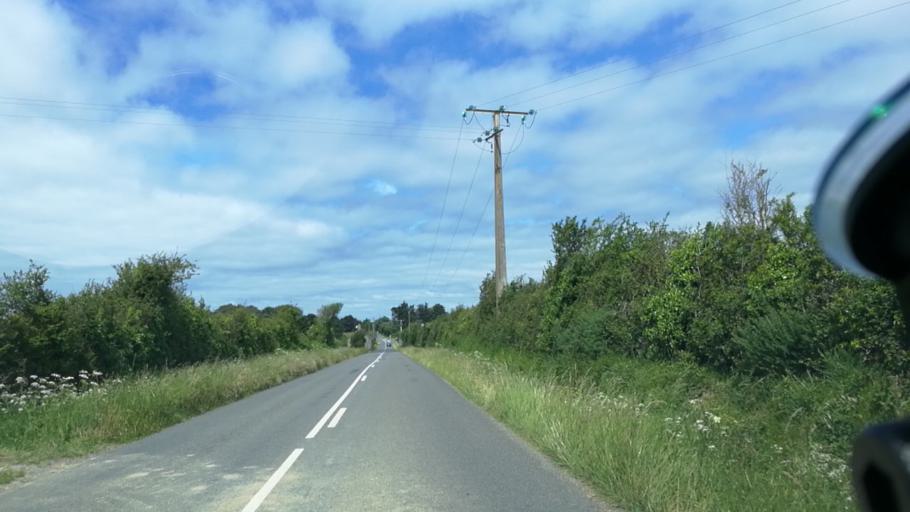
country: FR
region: Pays de la Loire
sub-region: Departement de la Loire-Atlantique
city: Mesquer
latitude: 47.4420
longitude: -2.4390
